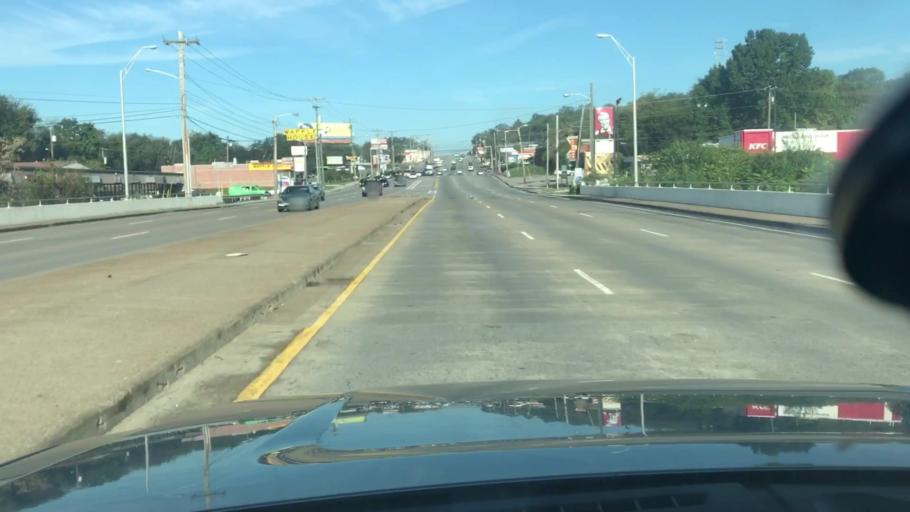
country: US
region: Tennessee
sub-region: Davidson County
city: Nashville
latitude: 36.1917
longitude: -86.8279
